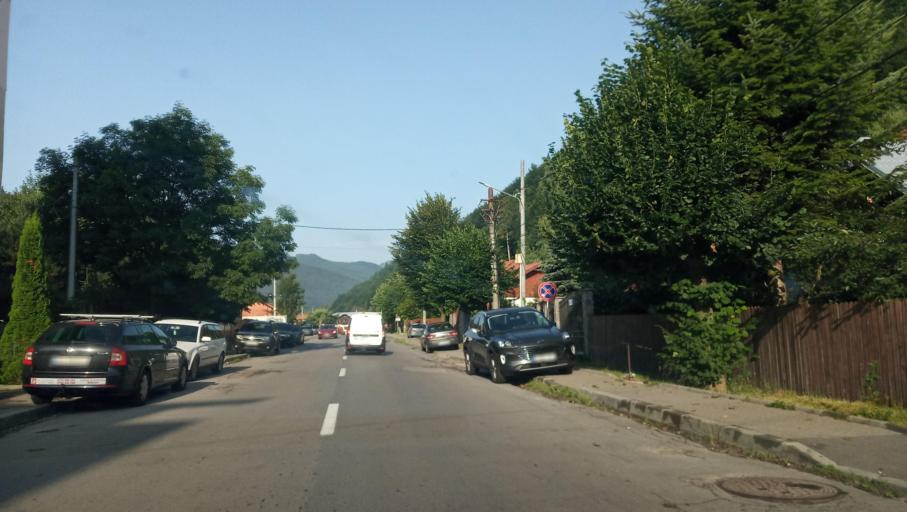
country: RO
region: Prahova
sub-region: Oras Sinaia
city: Sinaia
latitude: 45.3304
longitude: 25.5558
